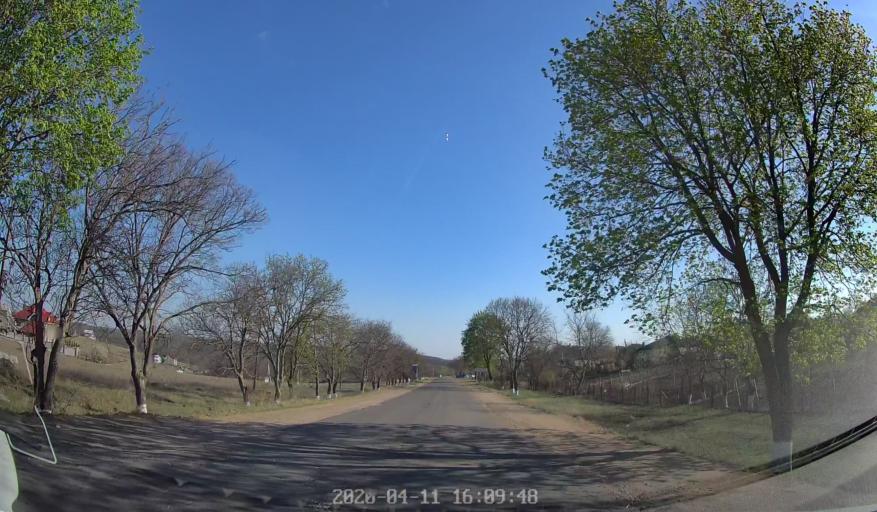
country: MD
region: Chisinau
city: Vadul lui Voda
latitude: 47.0715
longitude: 29.1367
